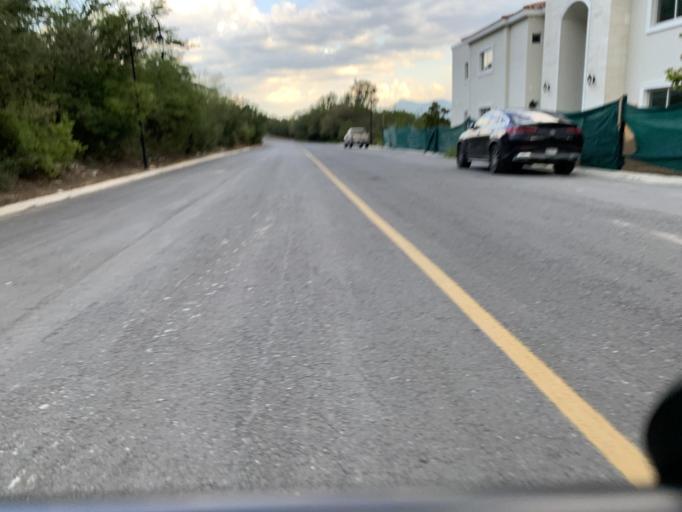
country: MX
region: Nuevo Leon
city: Santiago
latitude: 25.5105
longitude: -100.1810
